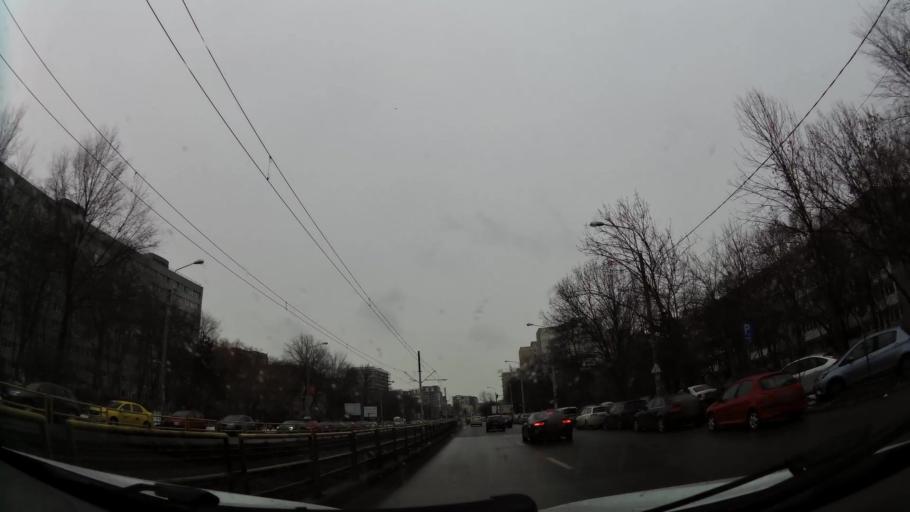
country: RO
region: Ilfov
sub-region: Comuna Chiajna
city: Rosu
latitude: 44.4240
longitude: 26.0345
